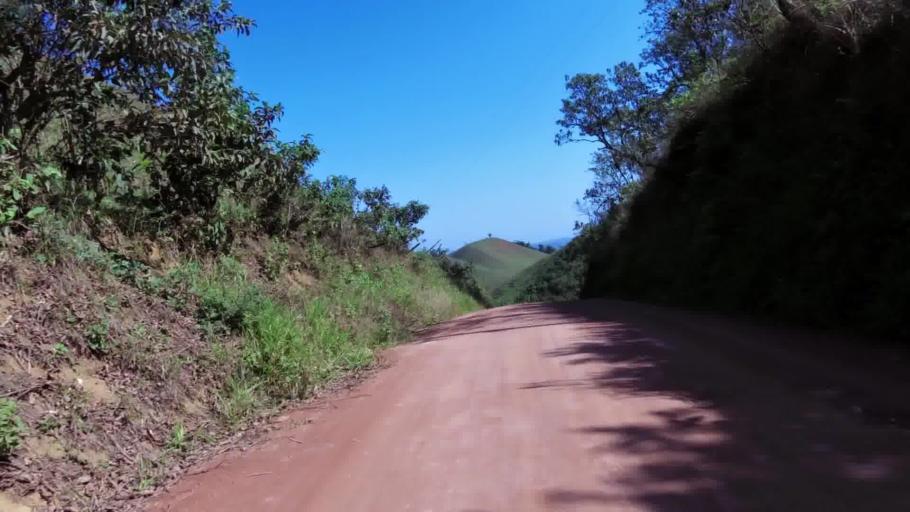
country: BR
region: Espirito Santo
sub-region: Alfredo Chaves
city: Alfredo Chaves
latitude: -20.5644
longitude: -40.7762
